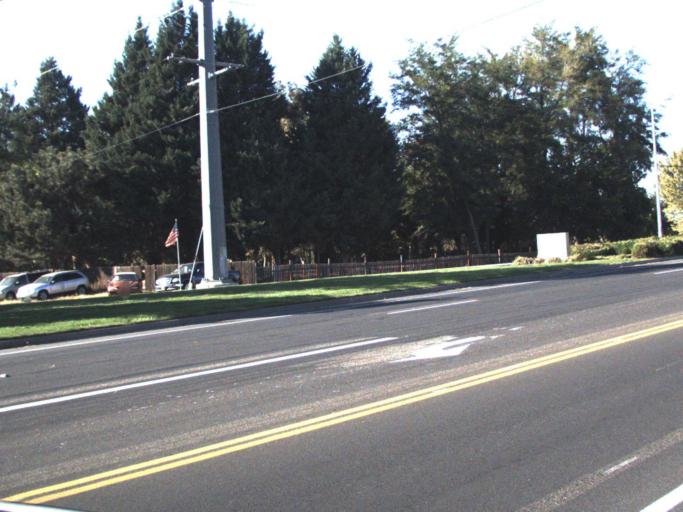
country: US
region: Washington
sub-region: Franklin County
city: Pasco
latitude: 46.2125
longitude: -119.1073
